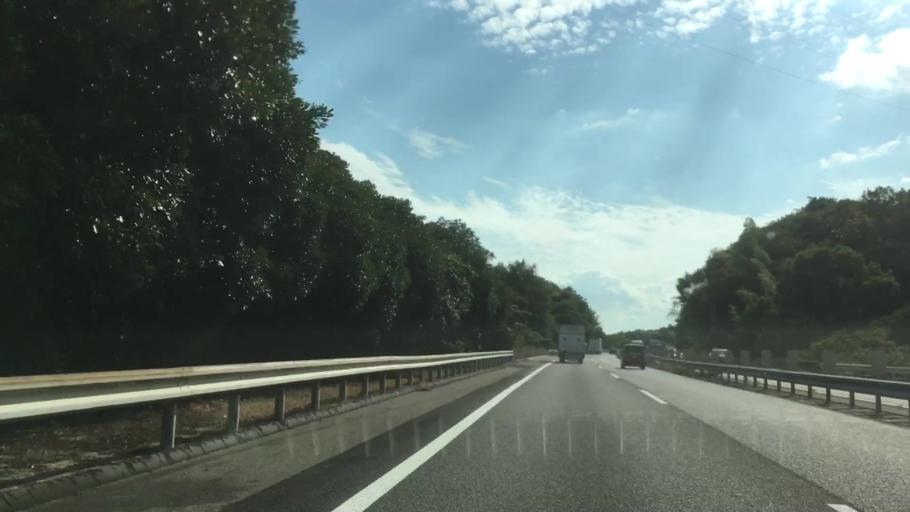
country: JP
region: Hiroshima
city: Ono-hara
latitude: 34.2813
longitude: 132.2593
